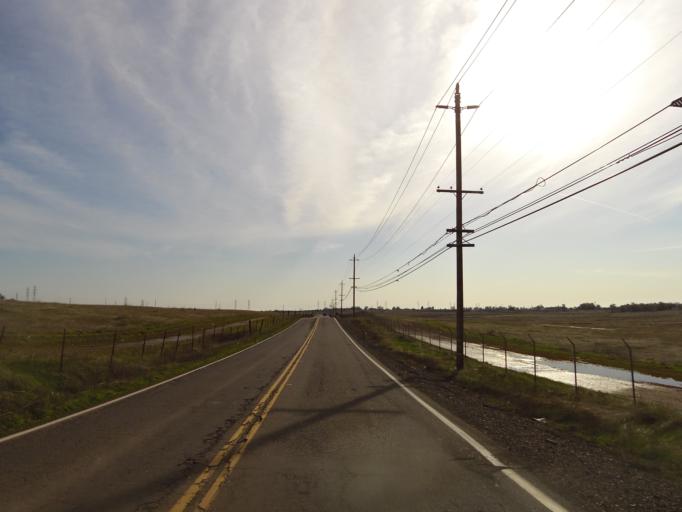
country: US
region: California
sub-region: Sacramento County
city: Folsom
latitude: 38.6209
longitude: -121.1505
